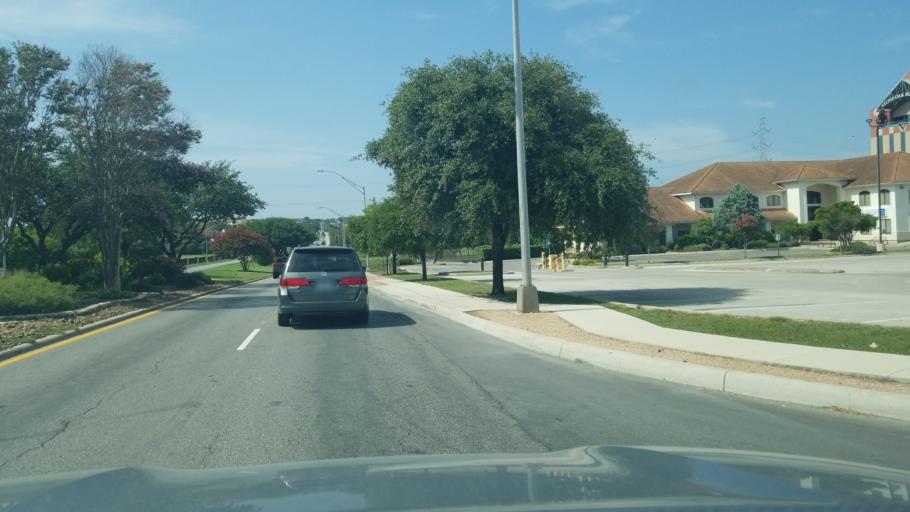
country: US
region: Texas
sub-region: Bexar County
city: Hollywood Park
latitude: 29.6191
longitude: -98.4942
